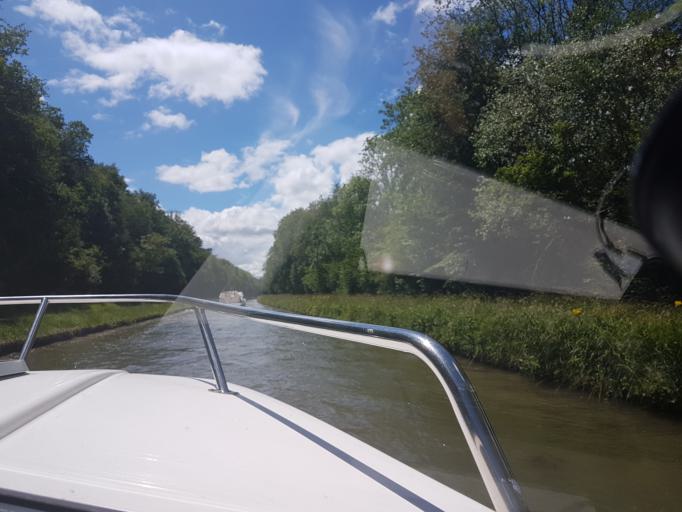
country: FR
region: Bourgogne
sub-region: Departement de l'Yonne
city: Vermenton
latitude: 47.5950
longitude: 3.6708
